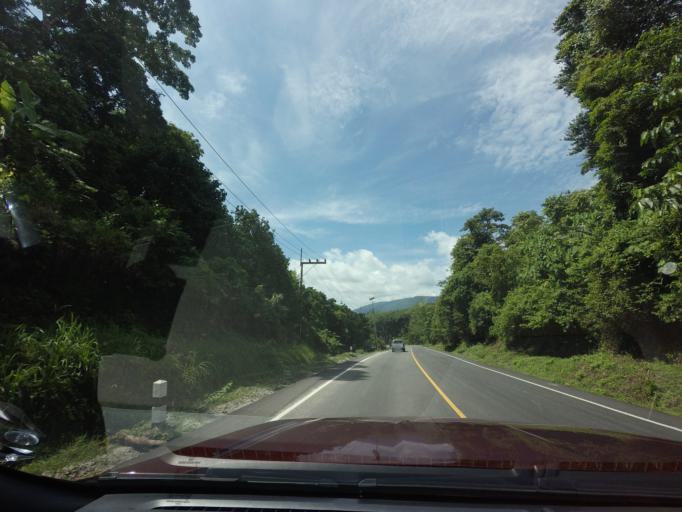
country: TH
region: Narathiwat
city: Rueso
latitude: 6.3609
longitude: 101.5556
